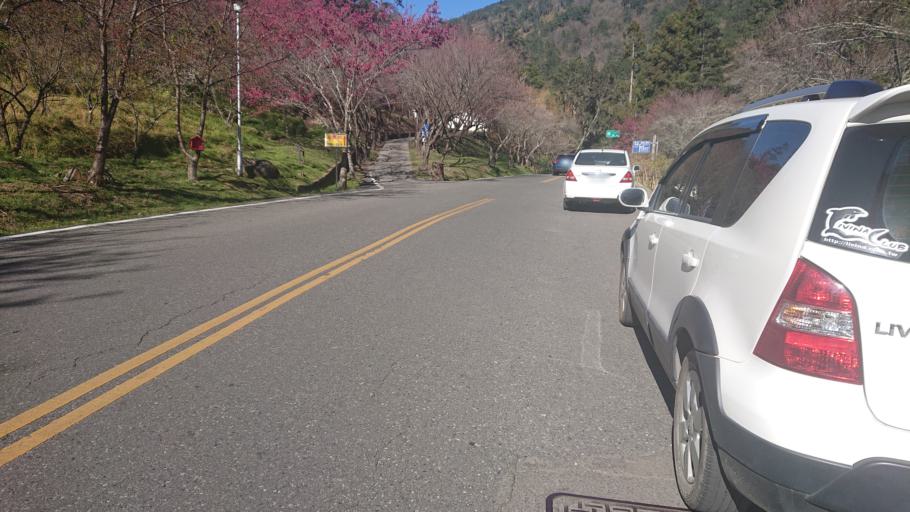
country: TW
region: Taiwan
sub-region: Hualien
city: Hualian
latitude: 24.3542
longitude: 121.3108
